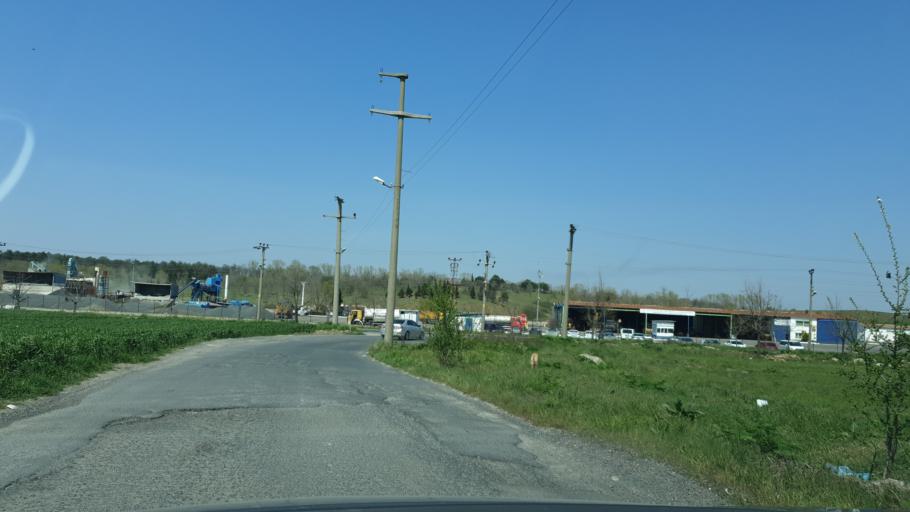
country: TR
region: Tekirdag
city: Corlu
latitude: 41.1678
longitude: 27.7897
